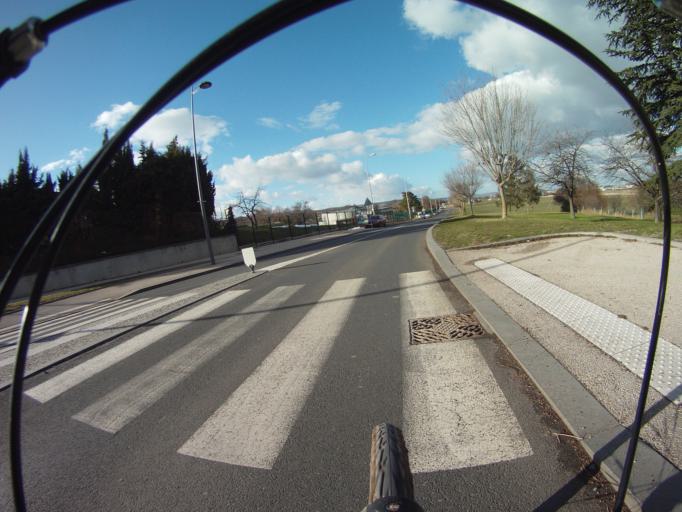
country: FR
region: Auvergne
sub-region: Departement du Puy-de-Dome
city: Perignat-les-Sarlieve
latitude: 45.7401
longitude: 3.1402
